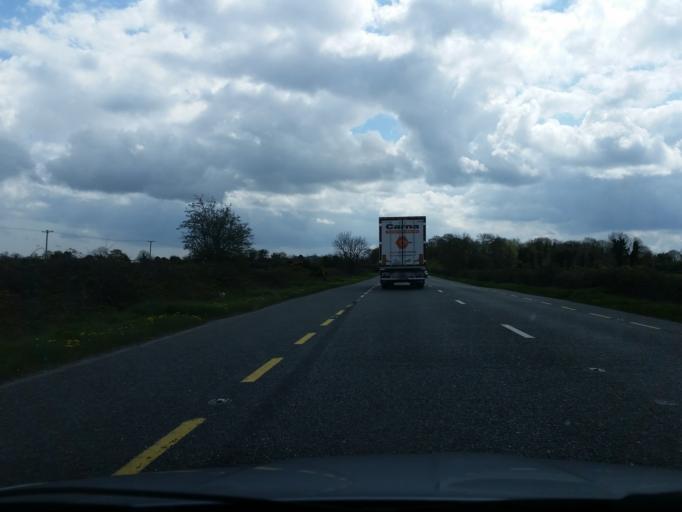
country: IE
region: Leinster
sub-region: An Mhi
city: Ashbourne
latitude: 53.5371
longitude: -6.4246
